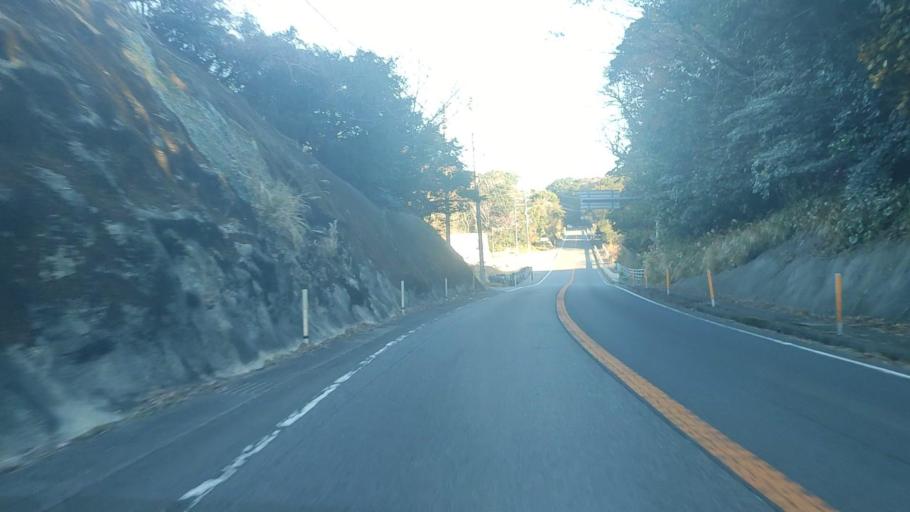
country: JP
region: Miyazaki
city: Nobeoka
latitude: 32.3480
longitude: 131.6225
